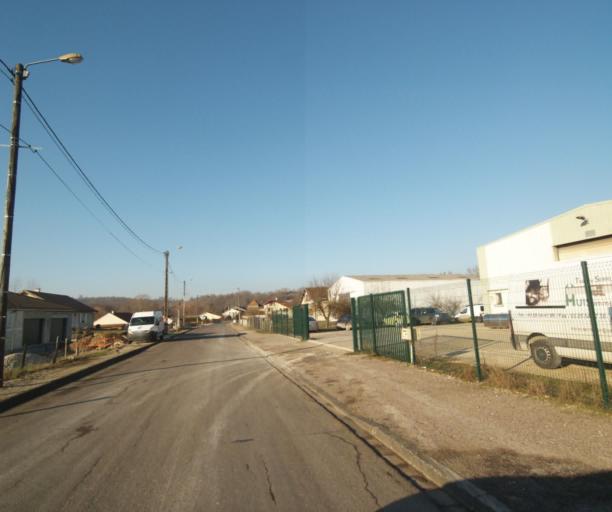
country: FR
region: Champagne-Ardenne
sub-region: Departement de la Haute-Marne
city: Chevillon
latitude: 48.5410
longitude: 5.1030
